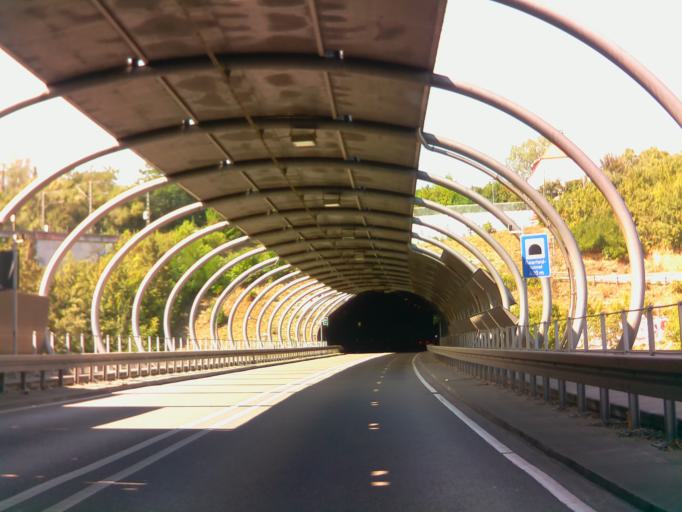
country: DE
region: Baden-Wuerttemberg
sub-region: Regierungsbezirk Stuttgart
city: Leinfelden-Echterdingen
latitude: 48.7337
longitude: 9.1214
